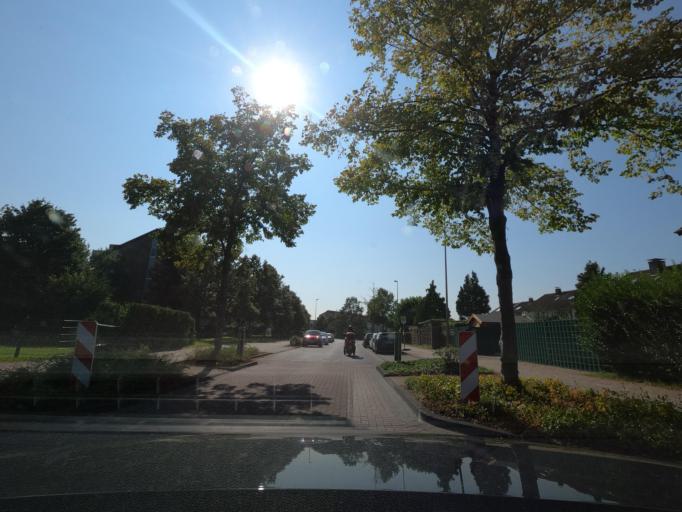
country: DE
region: North Rhine-Westphalia
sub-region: Regierungsbezirk Dusseldorf
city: Dinslaken
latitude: 51.5602
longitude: 6.7863
